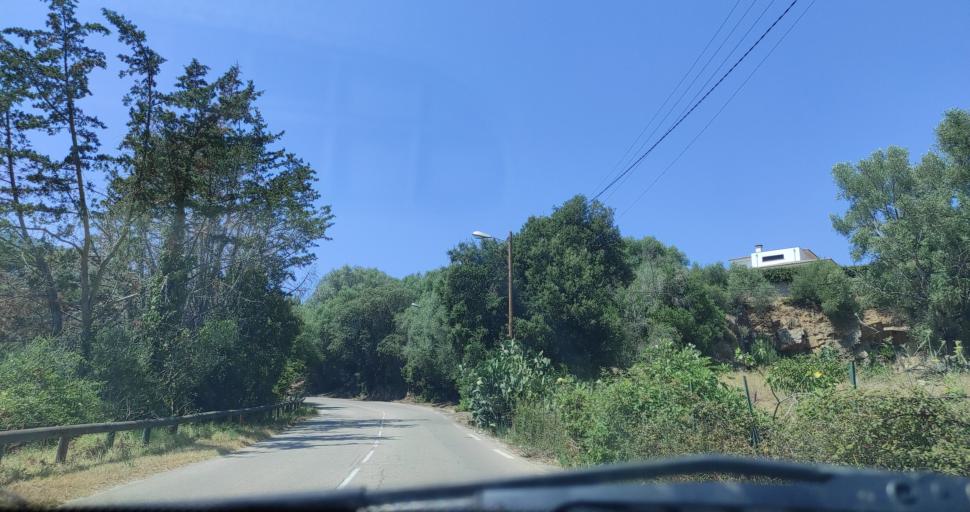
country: FR
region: Corsica
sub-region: Departement de la Corse-du-Sud
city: Ajaccio
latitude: 41.9475
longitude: 8.7364
